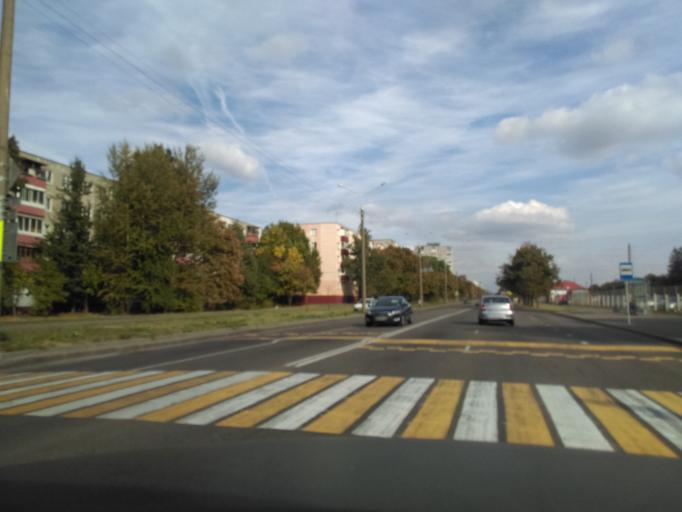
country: BY
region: Minsk
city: Hatava
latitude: 53.8343
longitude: 27.6175
